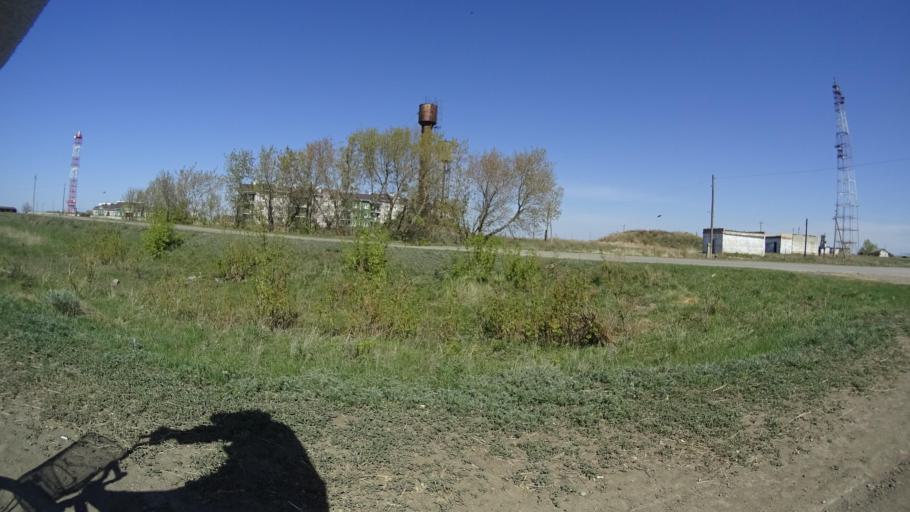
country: RU
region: Chelyabinsk
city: Chesma
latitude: 53.7908
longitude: 61.0405
